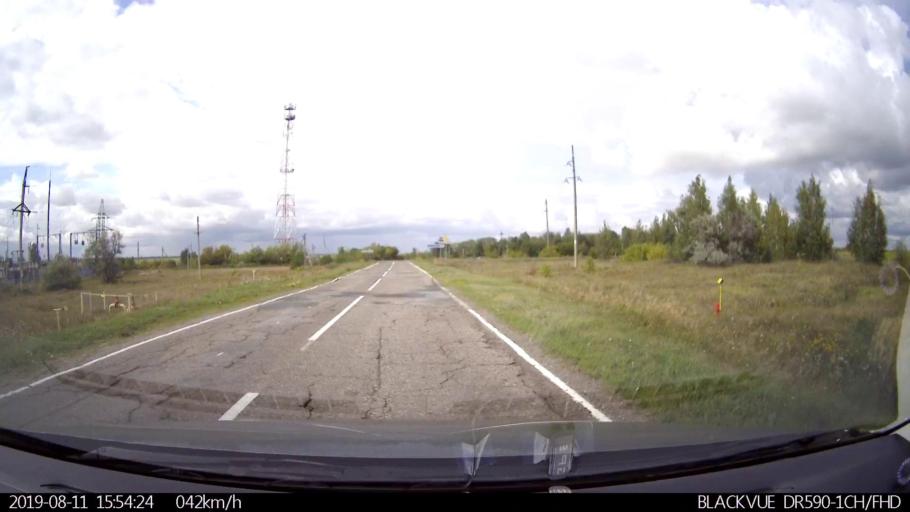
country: RU
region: Ulyanovsk
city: Ignatovka
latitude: 53.9410
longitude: 47.6565
